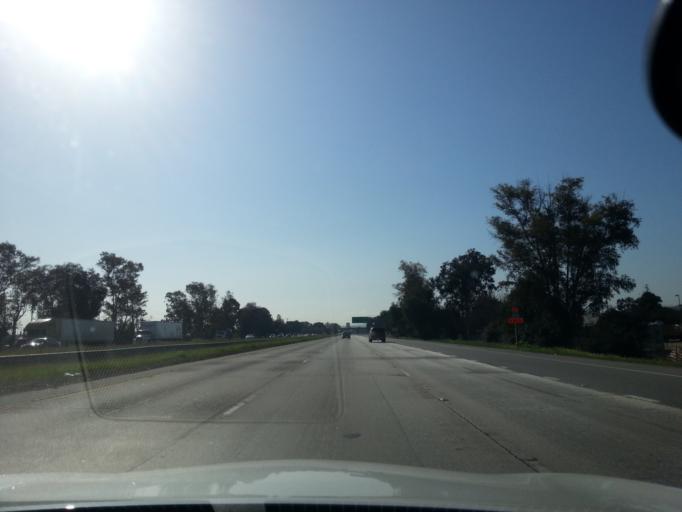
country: US
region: California
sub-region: Santa Clara County
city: Gilroy
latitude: 37.0090
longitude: -121.5596
